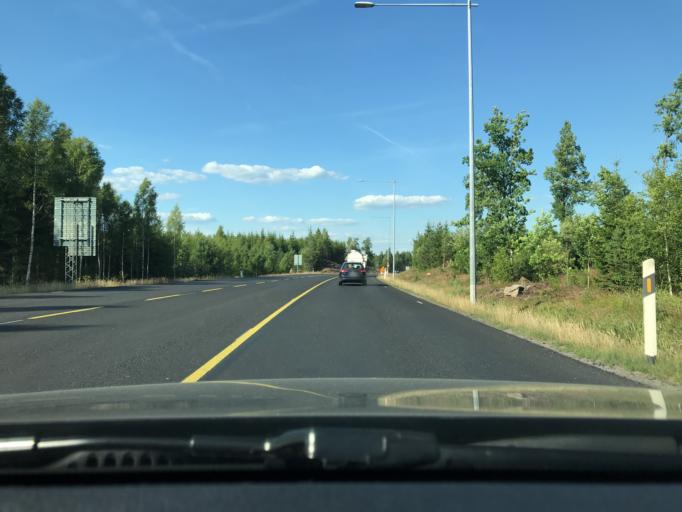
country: SE
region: Kronoberg
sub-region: Almhults Kommun
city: AElmhult
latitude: 56.5881
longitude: 14.1935
